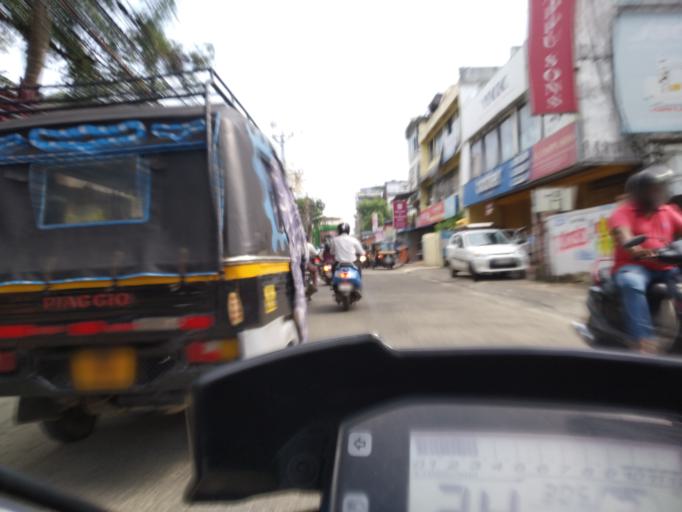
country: IN
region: Kerala
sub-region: Ernakulam
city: Cochin
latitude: 9.9830
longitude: 76.2840
